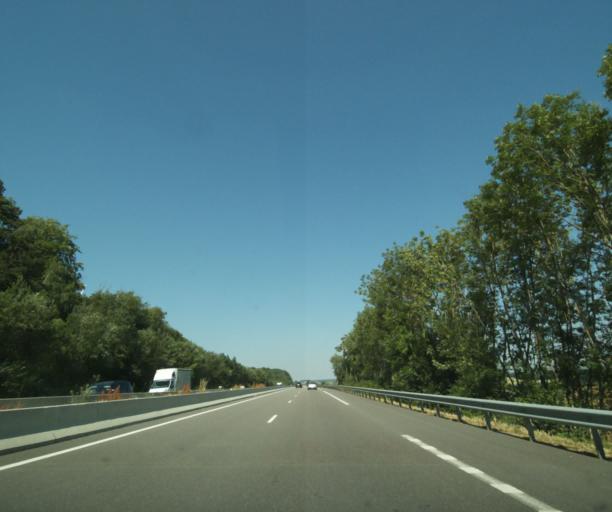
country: FR
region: Lorraine
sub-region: Departement de la Meuse
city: Lerouville
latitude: 48.7049
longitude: 5.5077
